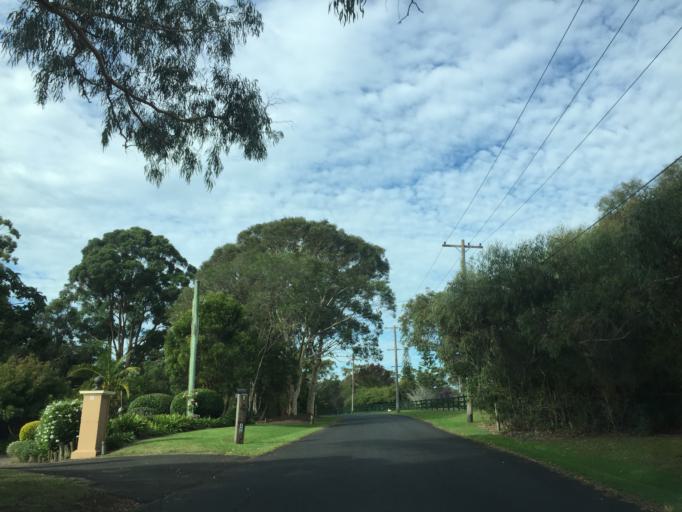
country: AU
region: New South Wales
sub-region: Hornsby Shire
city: Hornsby Heights
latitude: -33.6451
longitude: 151.0788
